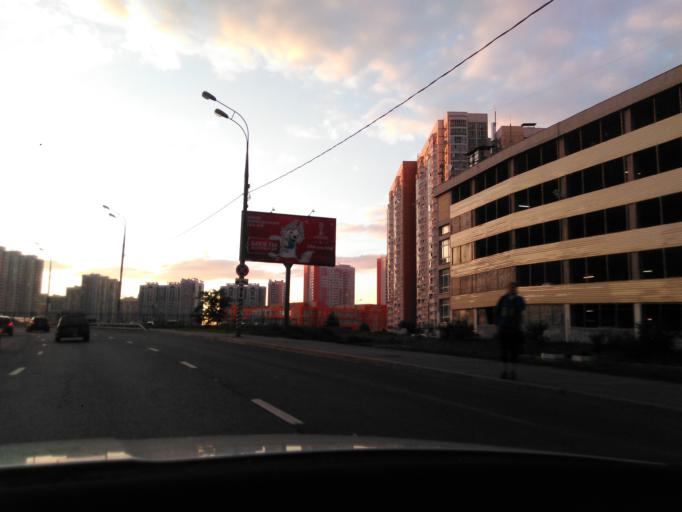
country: RU
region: Moscow
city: Khimki
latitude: 55.9000
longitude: 37.3986
